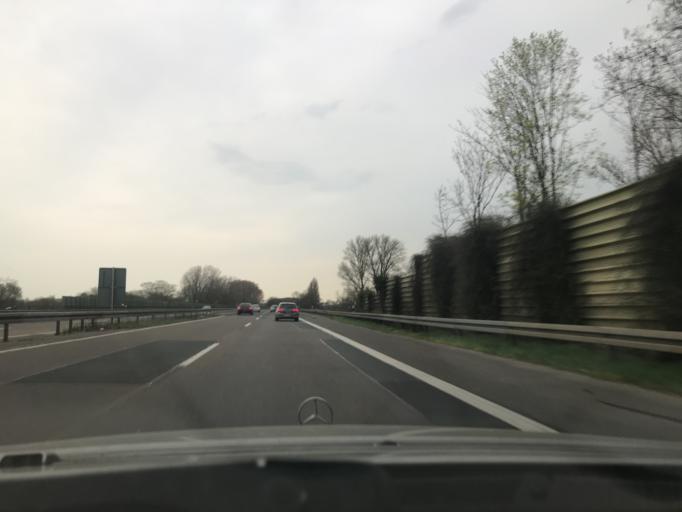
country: DE
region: North Rhine-Westphalia
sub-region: Regierungsbezirk Dusseldorf
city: Korschenbroich
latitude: 51.2291
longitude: 6.4898
